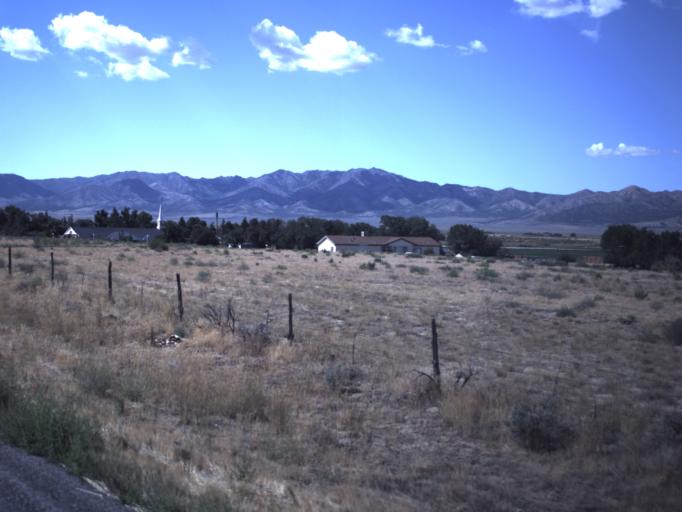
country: US
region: Utah
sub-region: Tooele County
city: Tooele
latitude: 40.0988
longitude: -112.4308
